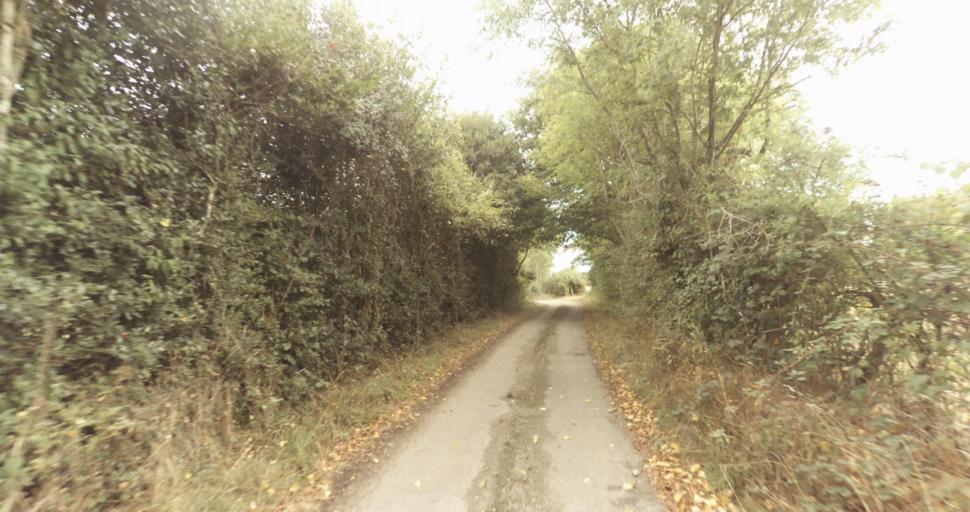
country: FR
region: Lower Normandy
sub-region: Departement de l'Orne
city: Gace
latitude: 48.8683
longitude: 0.3090
